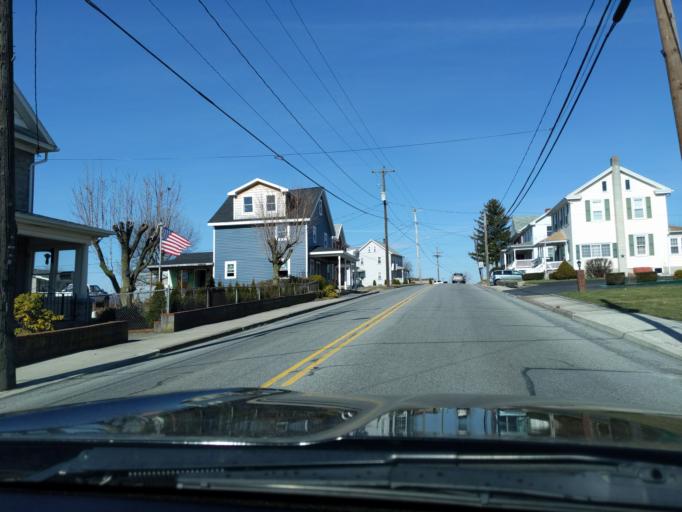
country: US
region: Pennsylvania
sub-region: Blair County
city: Martinsburg
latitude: 40.3150
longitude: -78.3316
